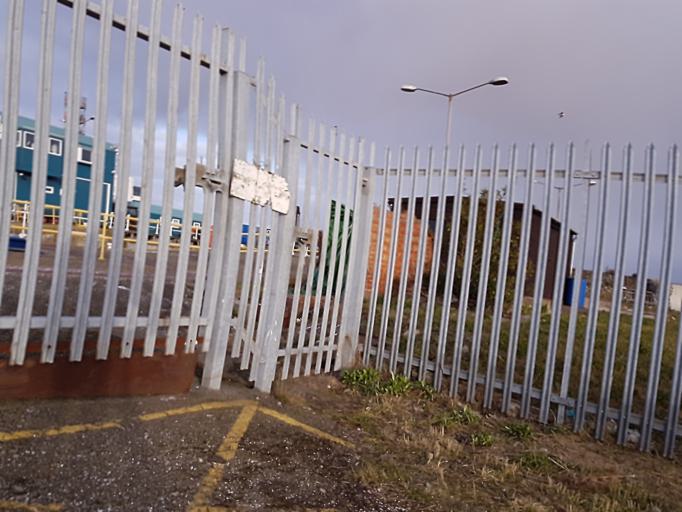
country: GB
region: England
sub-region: North East Lincolnshire
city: Grimsby
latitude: 53.5823
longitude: -0.0652
